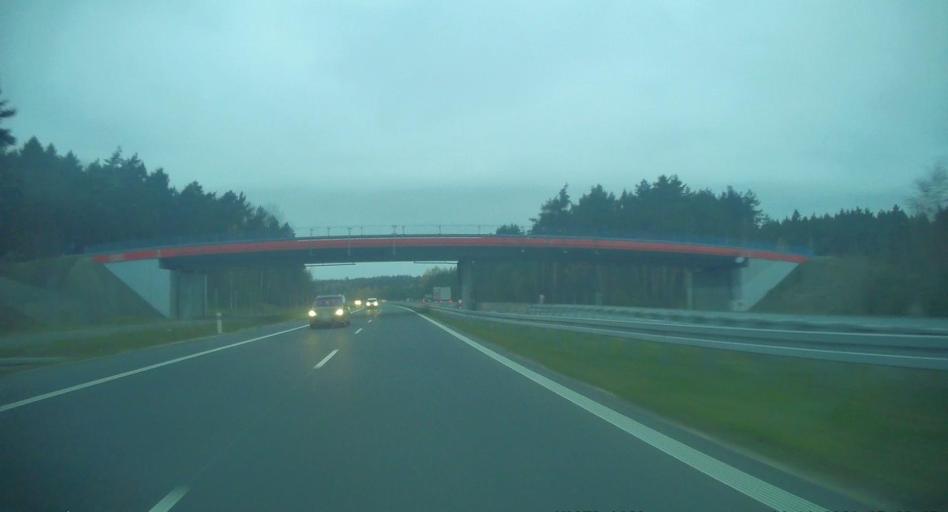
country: PL
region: Silesian Voivodeship
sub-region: Powiat bedzinski
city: Mierzecice
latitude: 50.4535
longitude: 19.1082
